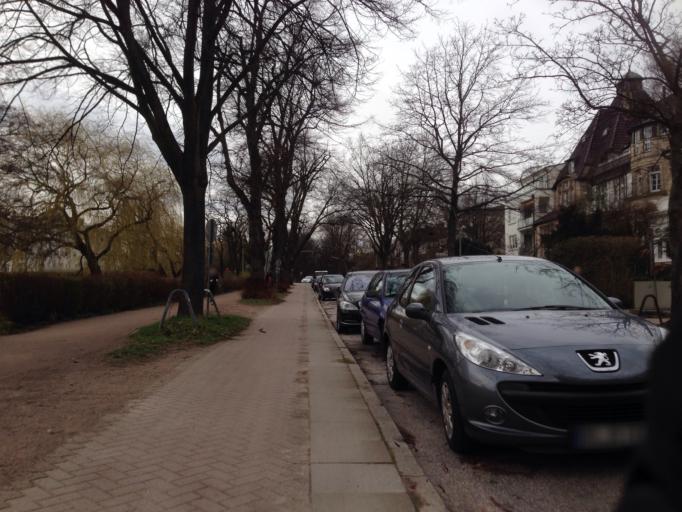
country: DE
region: Hamburg
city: Hamburg
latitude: 53.5797
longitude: 10.0035
